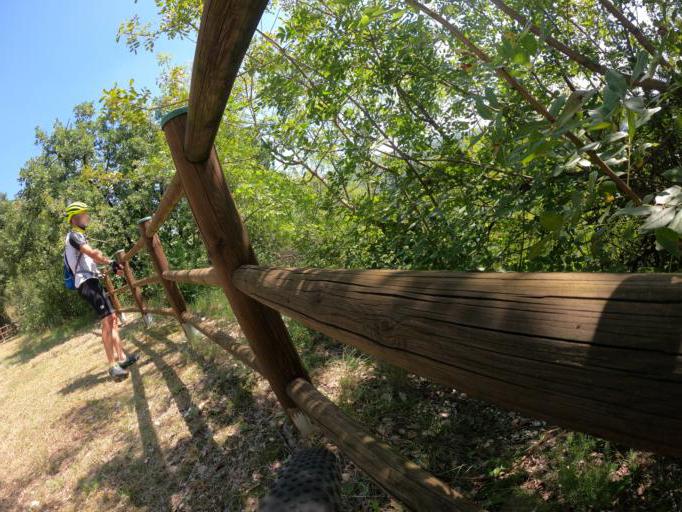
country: IT
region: Veneto
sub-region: Provincia di Verona
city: Volargne
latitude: 45.5552
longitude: 10.8224
